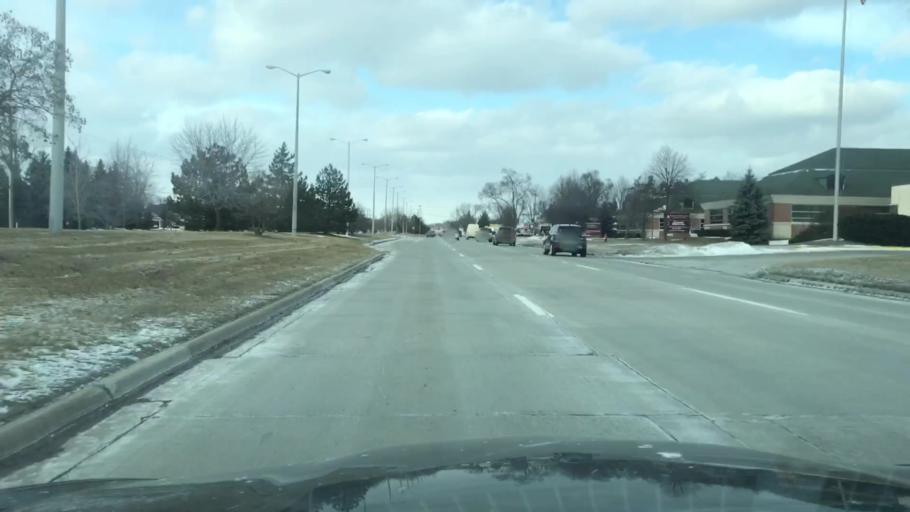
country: US
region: Michigan
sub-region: Macomb County
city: Utica
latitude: 42.6150
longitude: -83.0515
